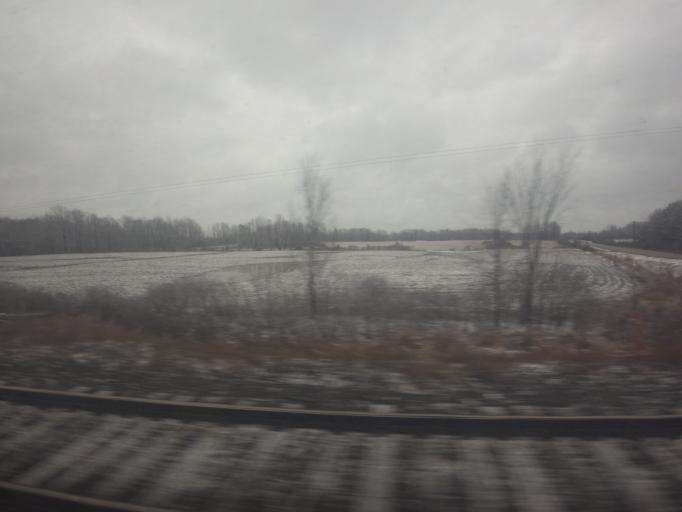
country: US
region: New York
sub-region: Jefferson County
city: Alexandria Bay
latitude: 44.4260
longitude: -75.9794
